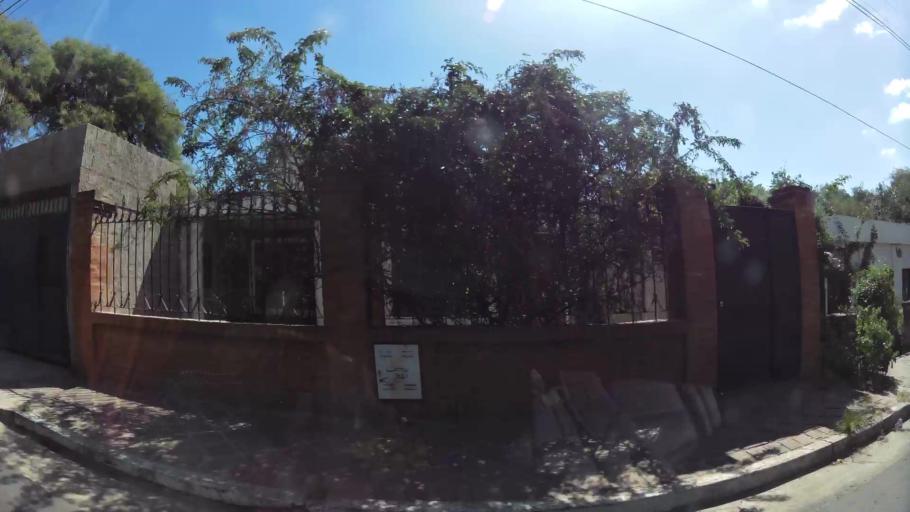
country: AR
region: Cordoba
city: Villa Allende
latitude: -31.2978
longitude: -64.3011
